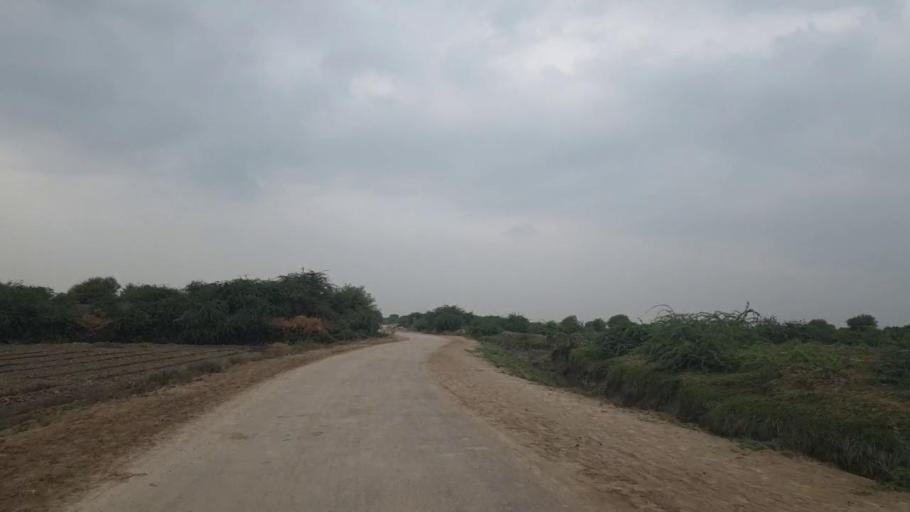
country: PK
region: Sindh
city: Badin
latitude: 24.6432
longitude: 68.6811
